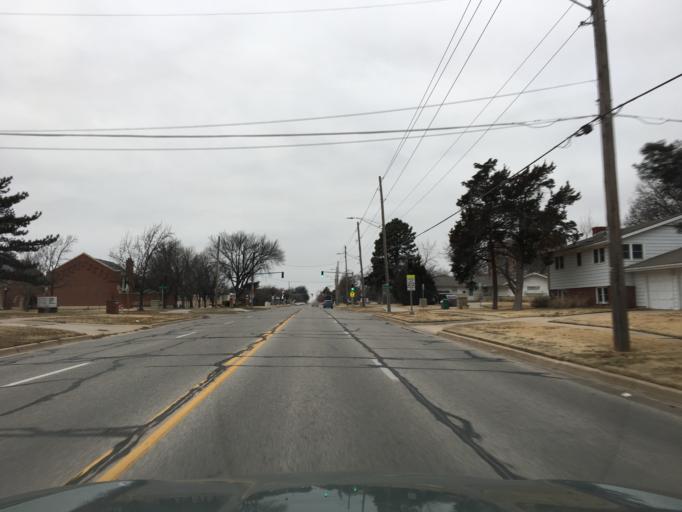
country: US
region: Kansas
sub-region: Sedgwick County
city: Bellaire
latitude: 37.7084
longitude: -97.2579
